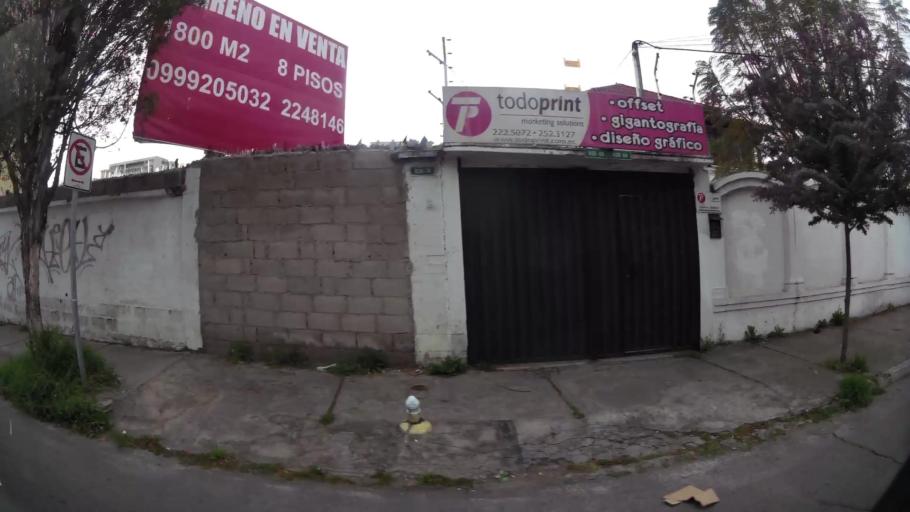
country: EC
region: Pichincha
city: Quito
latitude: -0.1999
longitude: -78.4874
